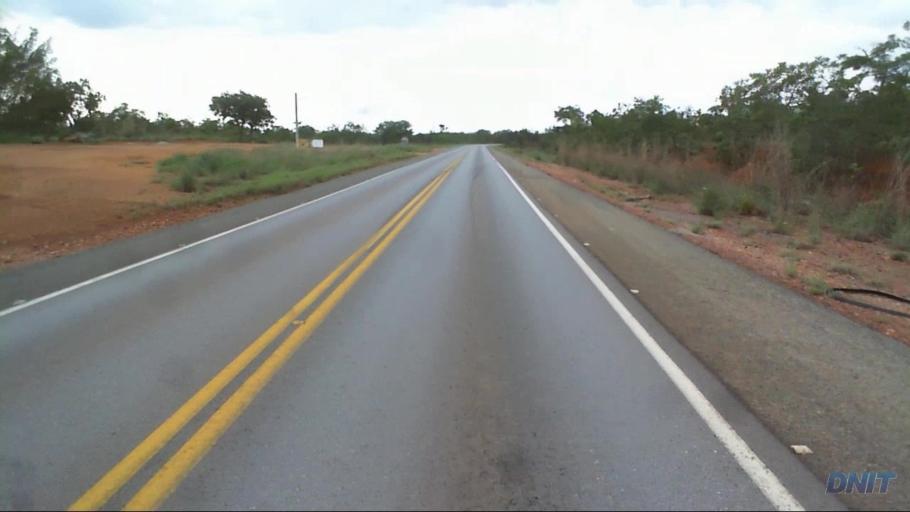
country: BR
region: Goias
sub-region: Barro Alto
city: Barro Alto
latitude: -14.7654
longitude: -49.0603
